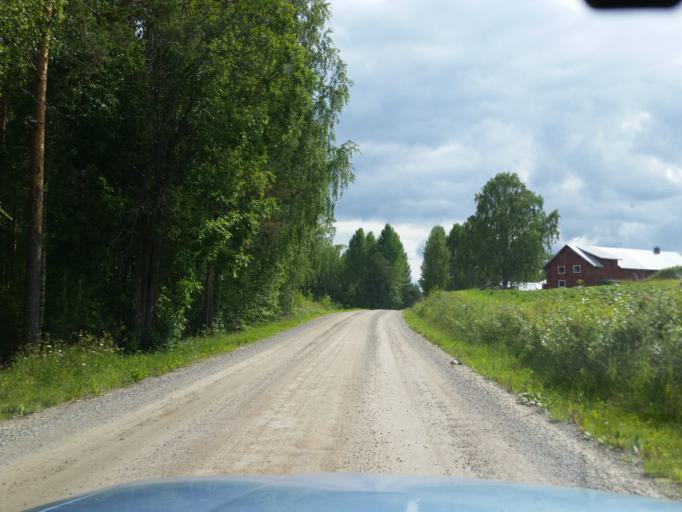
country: FI
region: Southern Savonia
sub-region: Savonlinna
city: Sulkava
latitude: 61.7300
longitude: 28.3186
